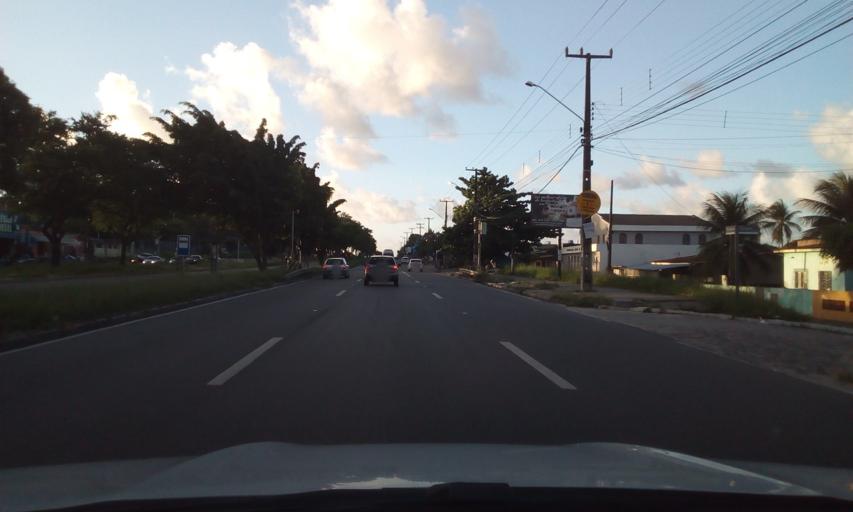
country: BR
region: Pernambuco
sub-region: Igarassu
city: Igarassu
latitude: -7.8626
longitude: -34.9076
